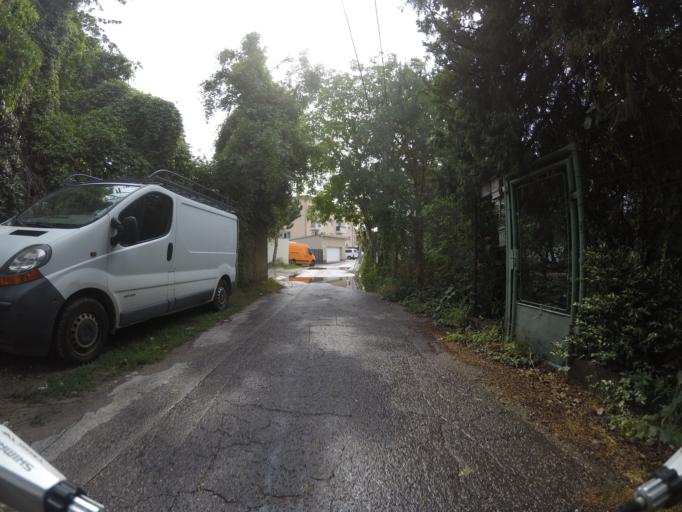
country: SK
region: Bratislavsky
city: Bratislava
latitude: 48.1481
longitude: 17.1550
